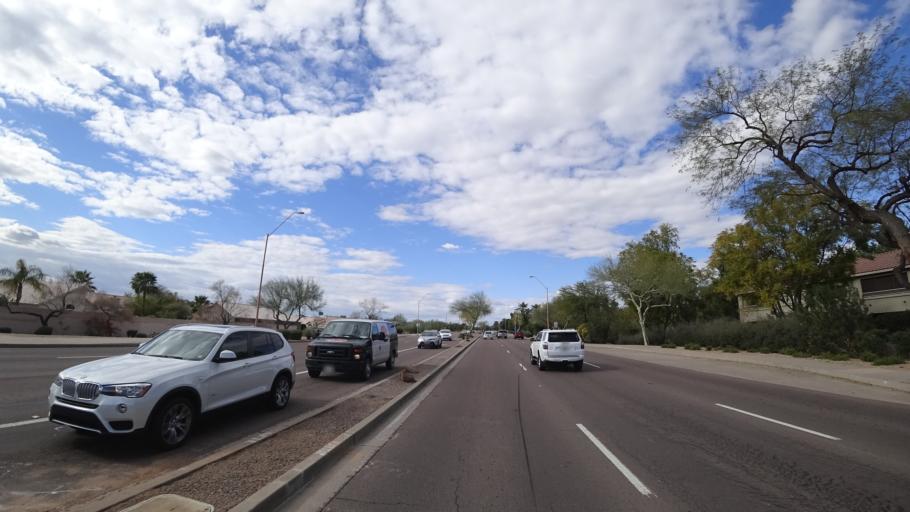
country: US
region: Arizona
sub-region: Maricopa County
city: Paradise Valley
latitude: 33.6219
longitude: -111.8756
